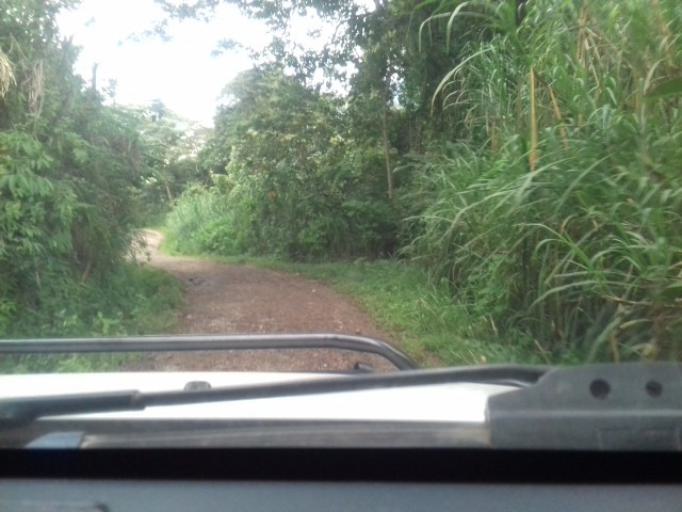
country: NI
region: Atlantico Norte (RAAN)
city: Waslala
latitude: 13.2093
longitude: -85.5785
